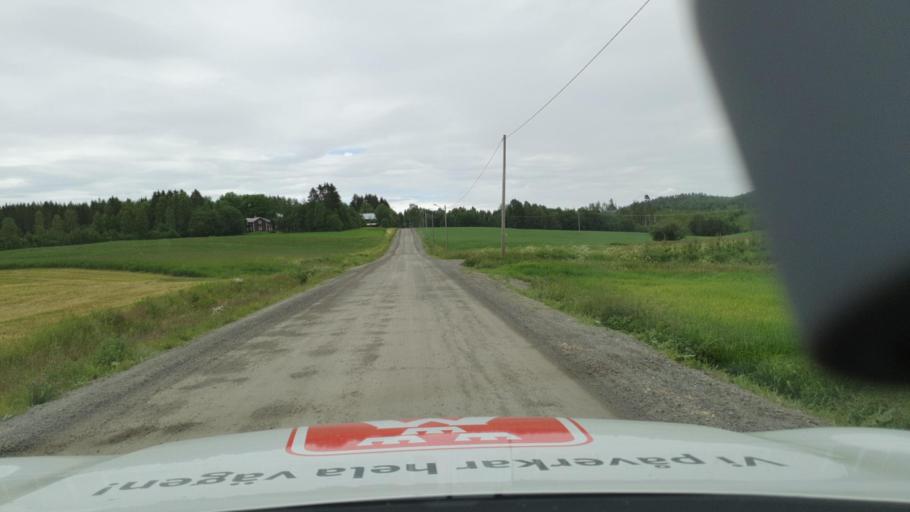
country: SE
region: Vaesterbotten
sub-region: Nordmalings Kommun
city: Nordmaling
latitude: 63.6457
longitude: 19.4276
